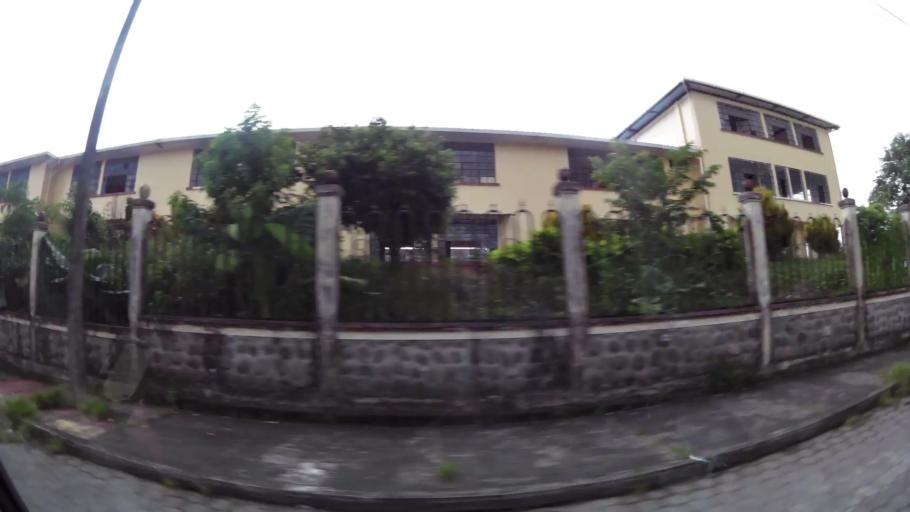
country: EC
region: Pastaza
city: Puyo
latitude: -1.4915
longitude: -77.9990
